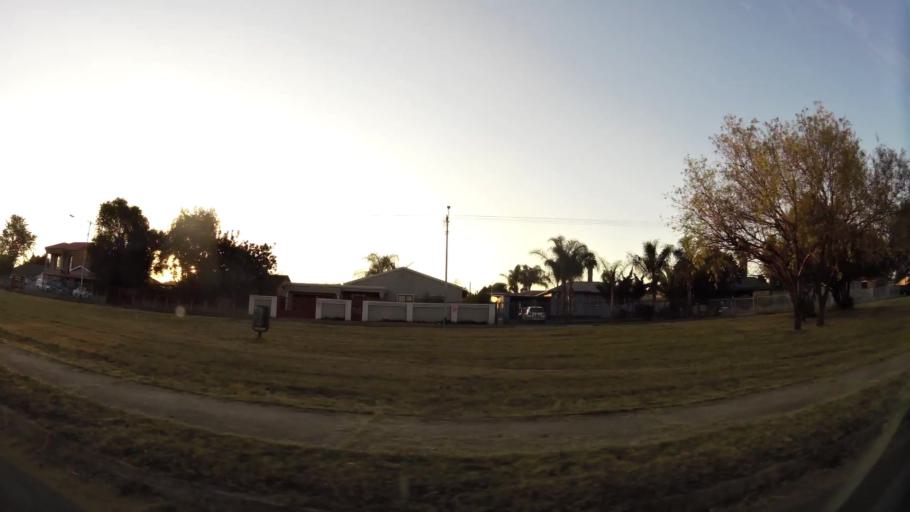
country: ZA
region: Gauteng
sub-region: City of Tshwane Metropolitan Municipality
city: Pretoria
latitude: -25.7466
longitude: 28.1286
